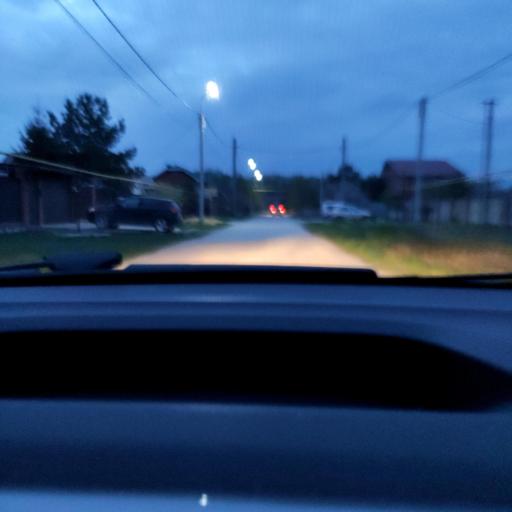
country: RU
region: Samara
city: Tol'yatti
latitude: 53.5511
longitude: 49.3992
